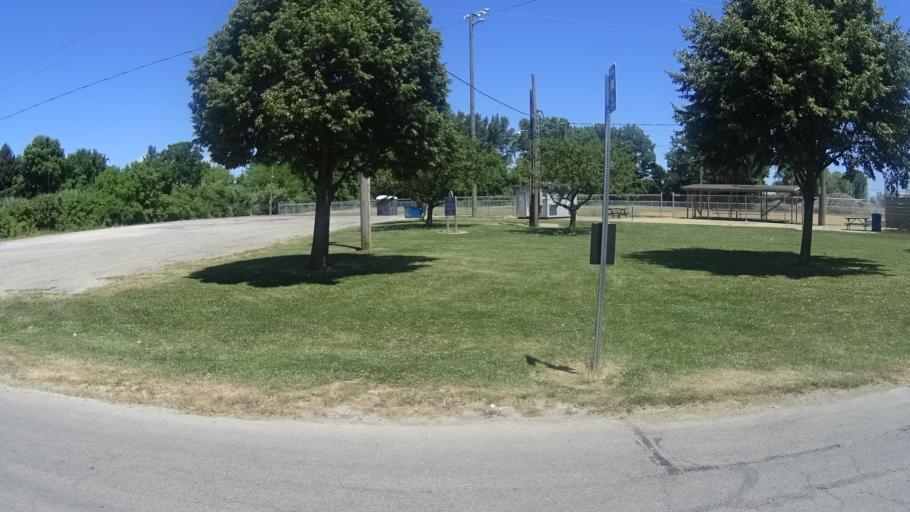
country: US
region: Ohio
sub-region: Erie County
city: Sandusky
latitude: 41.4501
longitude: -82.6733
